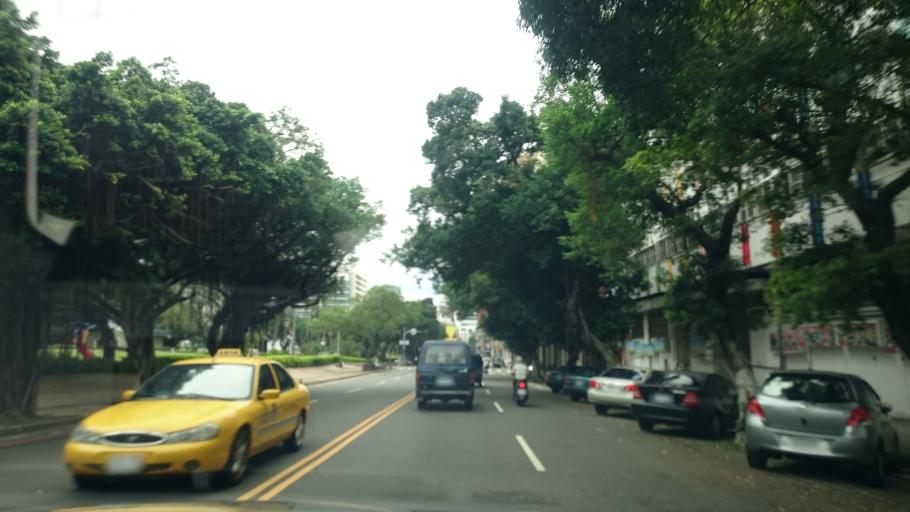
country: TW
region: Taiwan
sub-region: Taichung City
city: Taichung
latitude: 24.1443
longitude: 120.6821
